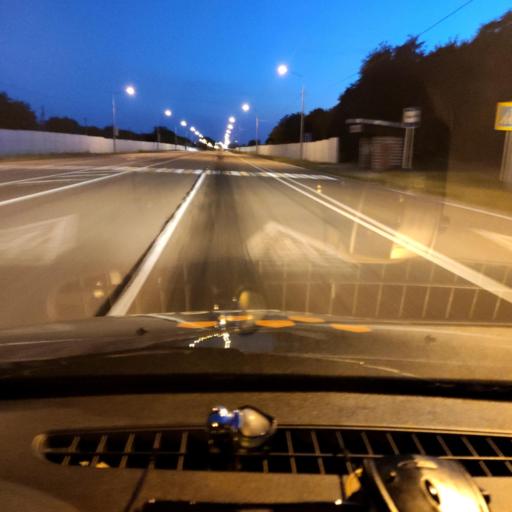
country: RU
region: Belgorod
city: Skorodnoye
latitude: 51.1859
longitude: 37.3631
